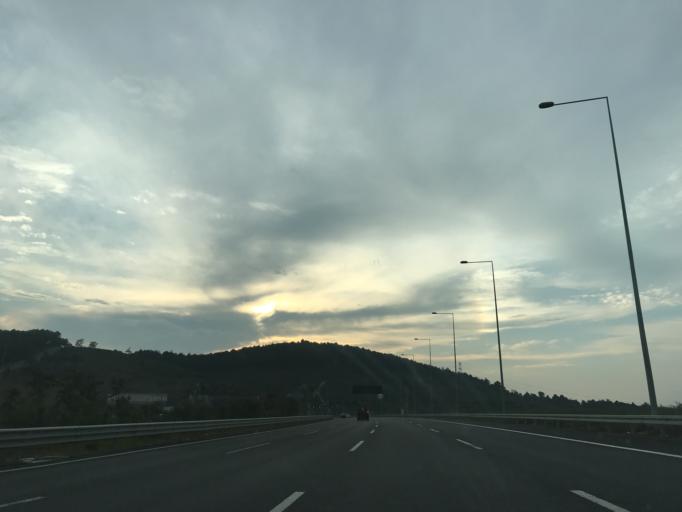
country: TR
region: Istanbul
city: Samandira
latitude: 41.0560
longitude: 29.1858
